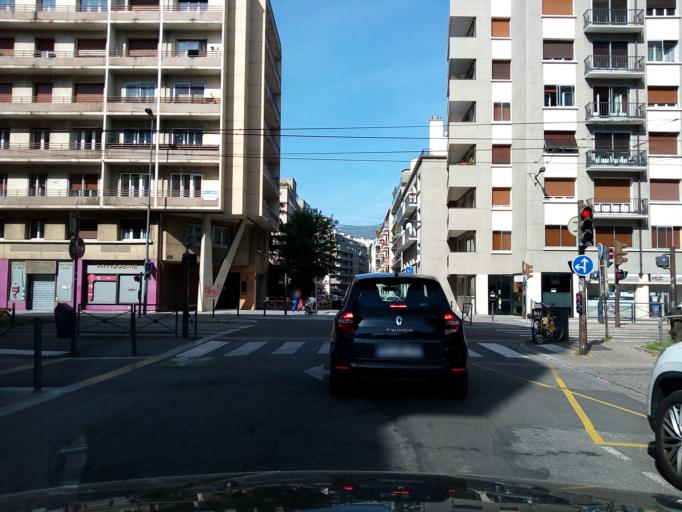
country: FR
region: Rhone-Alpes
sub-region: Departement de l'Isere
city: Grenoble
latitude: 45.1813
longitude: 5.7322
